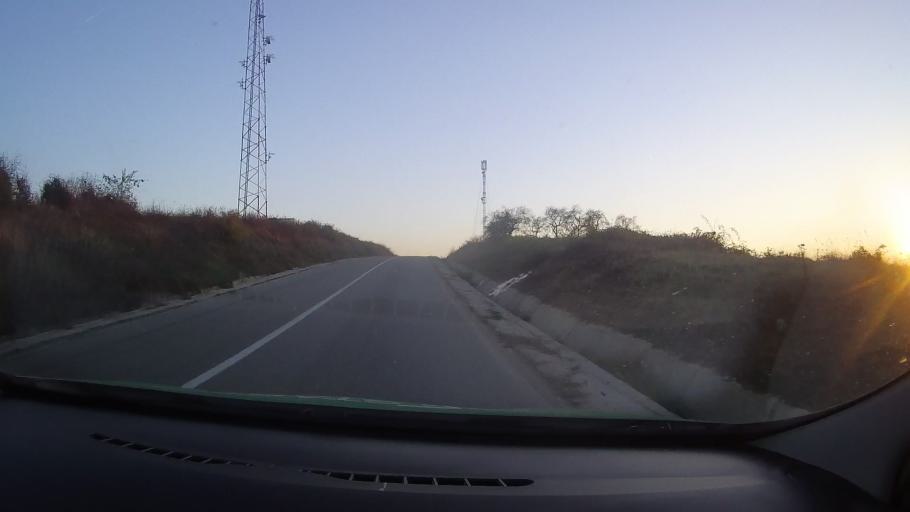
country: RO
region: Timis
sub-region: Comuna Manastiur
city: Manastiur
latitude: 45.8249
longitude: 22.0716
